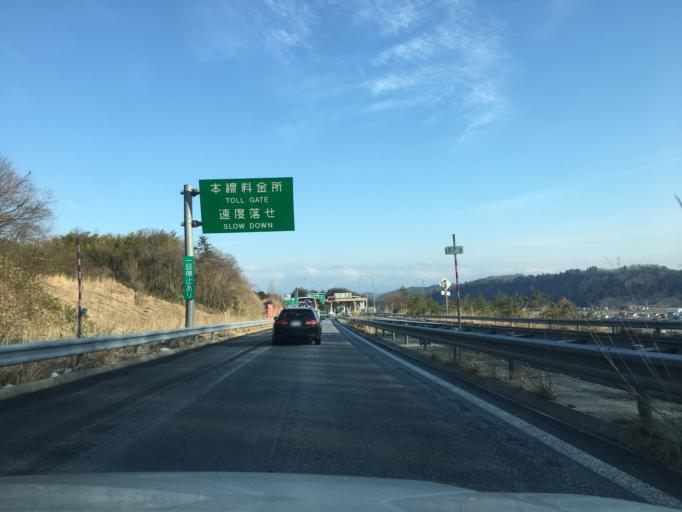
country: JP
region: Yamagata
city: Sagae
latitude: 38.4258
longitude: 140.1608
